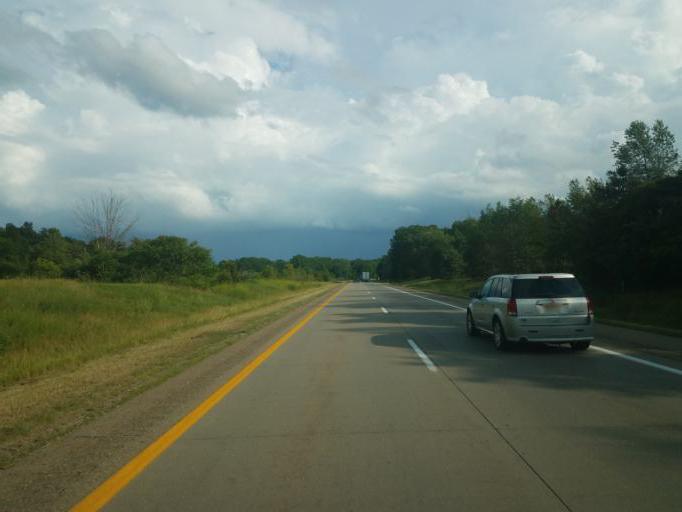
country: US
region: Michigan
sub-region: Calhoun County
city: Marshall
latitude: 42.1554
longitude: -84.9929
